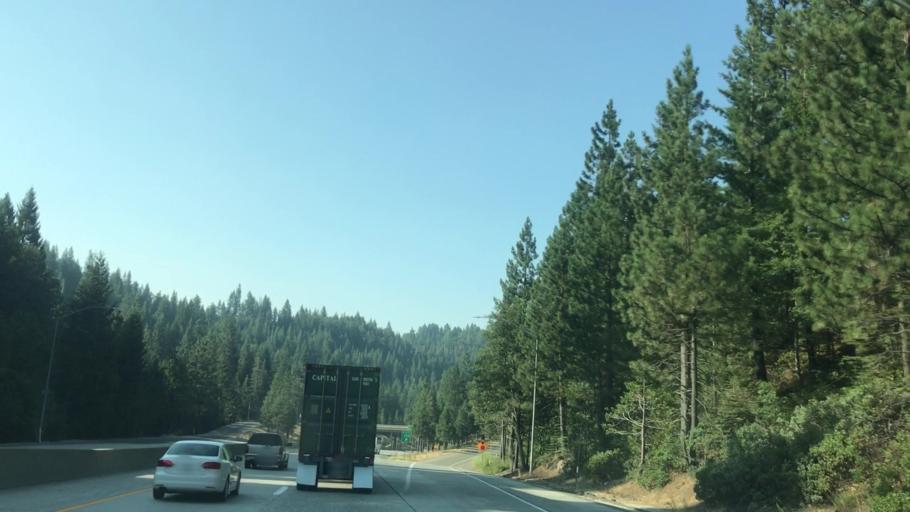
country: US
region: California
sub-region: Placer County
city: Foresthill
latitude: 39.2399
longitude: -120.7526
